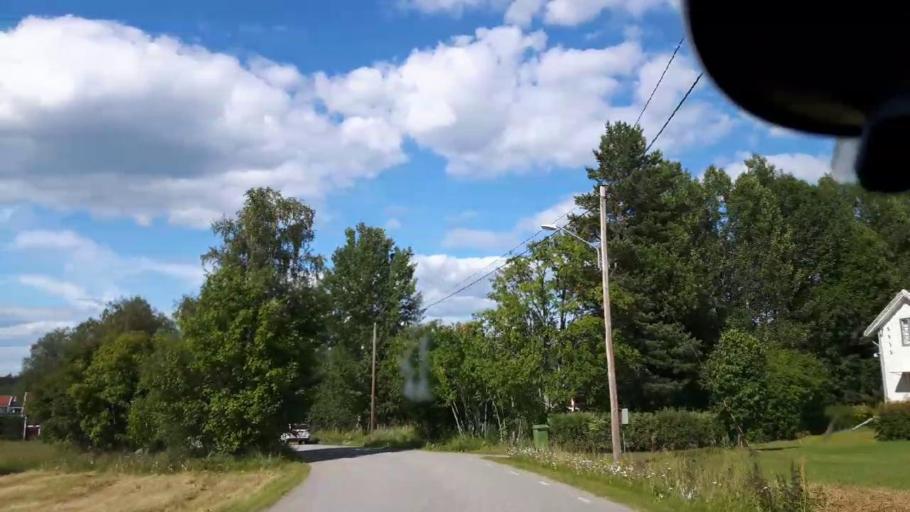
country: SE
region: Jaemtland
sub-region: Braecke Kommun
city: Braecke
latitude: 62.8785
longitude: 15.2756
